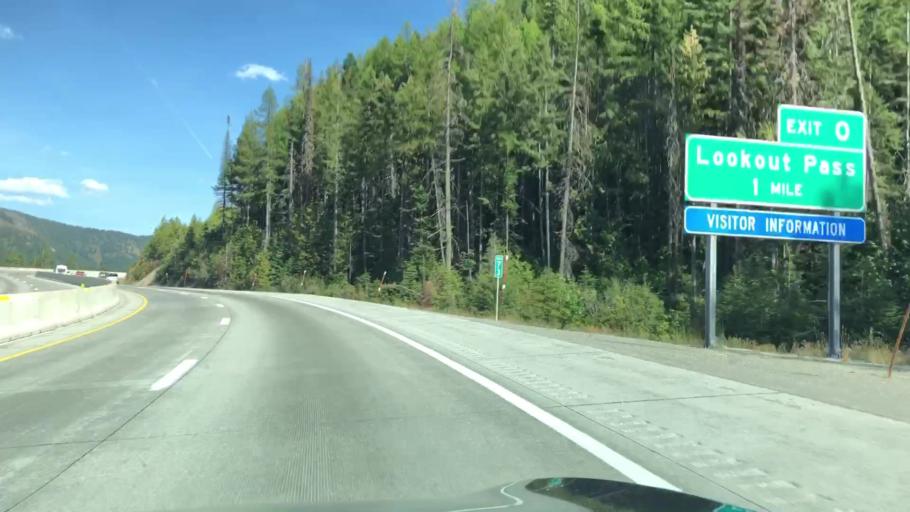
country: US
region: Idaho
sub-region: Shoshone County
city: Wallace
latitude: 47.4622
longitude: -115.7050
